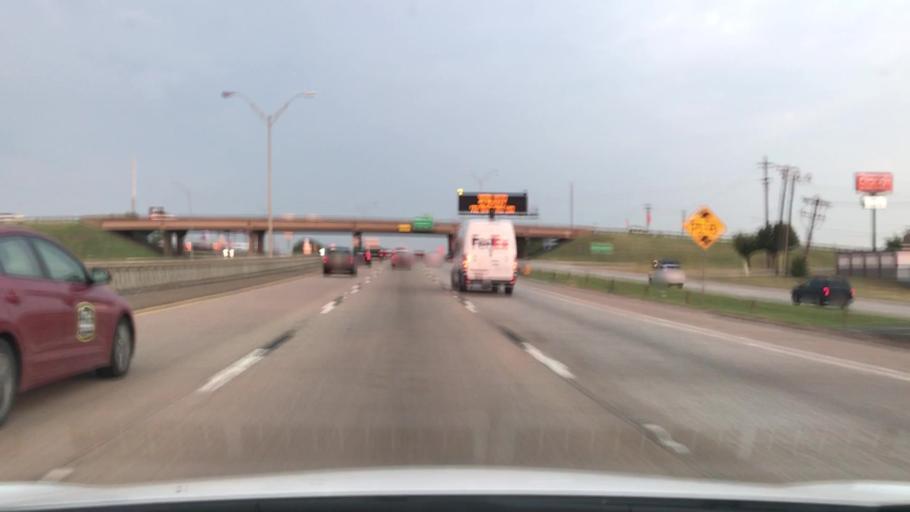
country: US
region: Texas
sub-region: Dallas County
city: Mesquite
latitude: 32.8192
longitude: -96.6372
